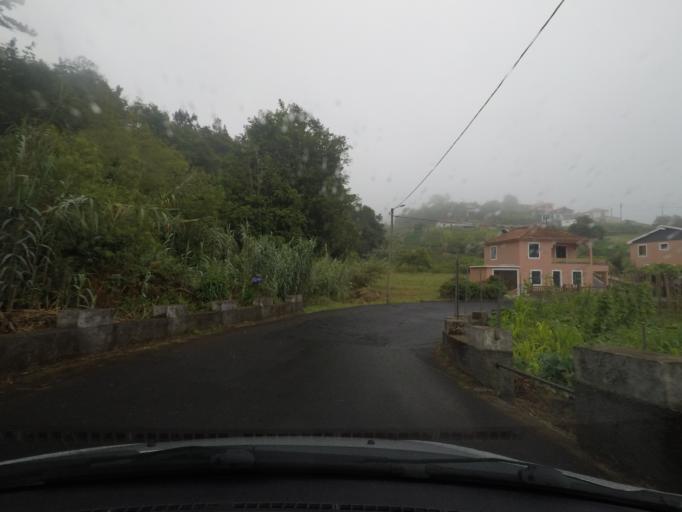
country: PT
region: Madeira
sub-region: Santana
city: Santana
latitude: 32.7944
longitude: -16.8740
